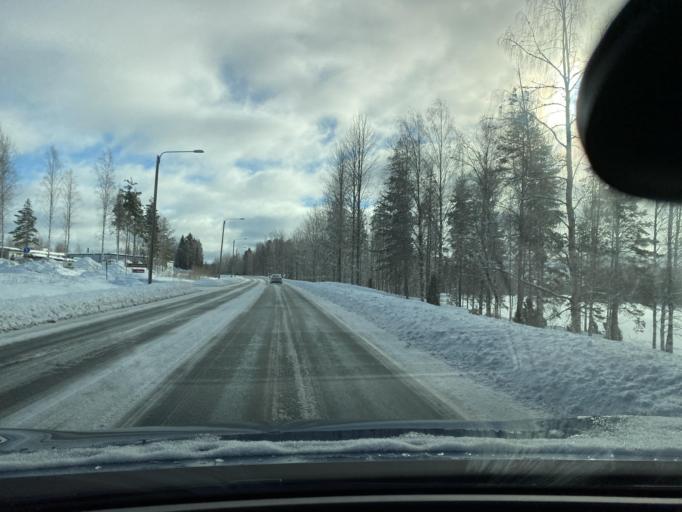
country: FI
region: Southern Savonia
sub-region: Mikkeli
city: Kangasniemi
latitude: 62.0080
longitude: 26.6411
